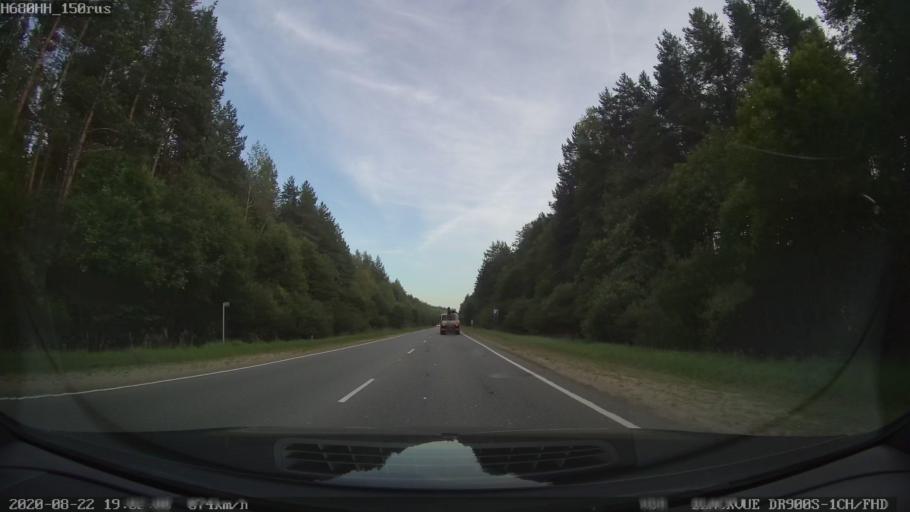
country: RU
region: Tverskaya
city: Vasil'yevskiy Mokh
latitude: 57.1132
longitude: 36.1180
